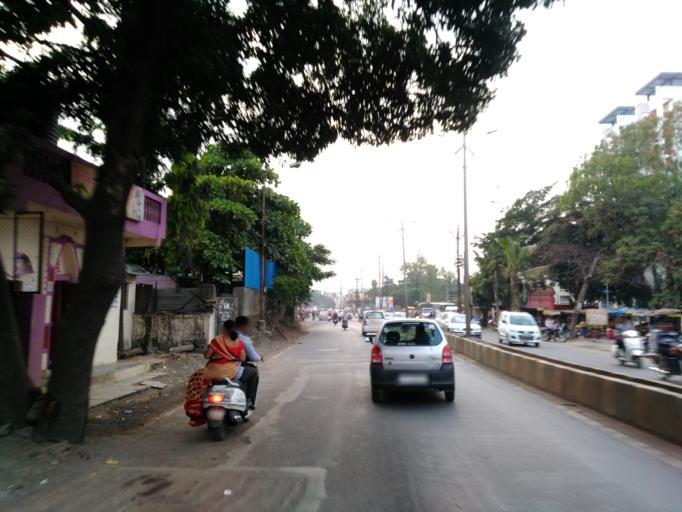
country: IN
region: Maharashtra
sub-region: Pune Division
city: Pune
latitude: 18.4500
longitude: 73.8767
